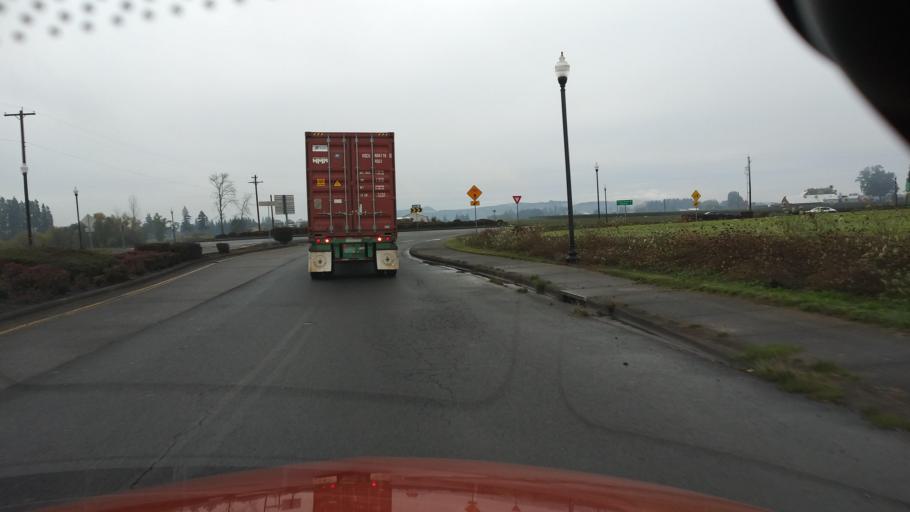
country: US
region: Oregon
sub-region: Washington County
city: Cornelius
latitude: 45.5523
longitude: -123.0643
